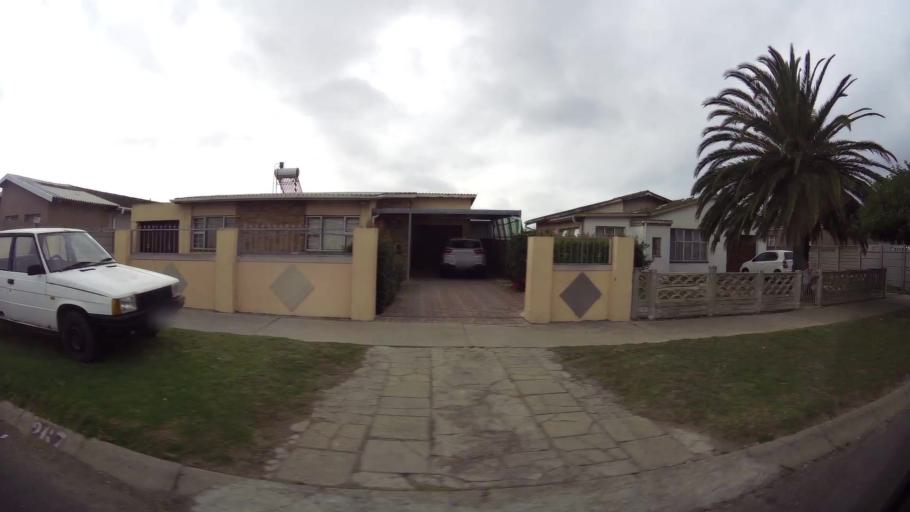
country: ZA
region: Eastern Cape
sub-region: Nelson Mandela Bay Metropolitan Municipality
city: Port Elizabeth
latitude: -33.9012
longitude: 25.5531
